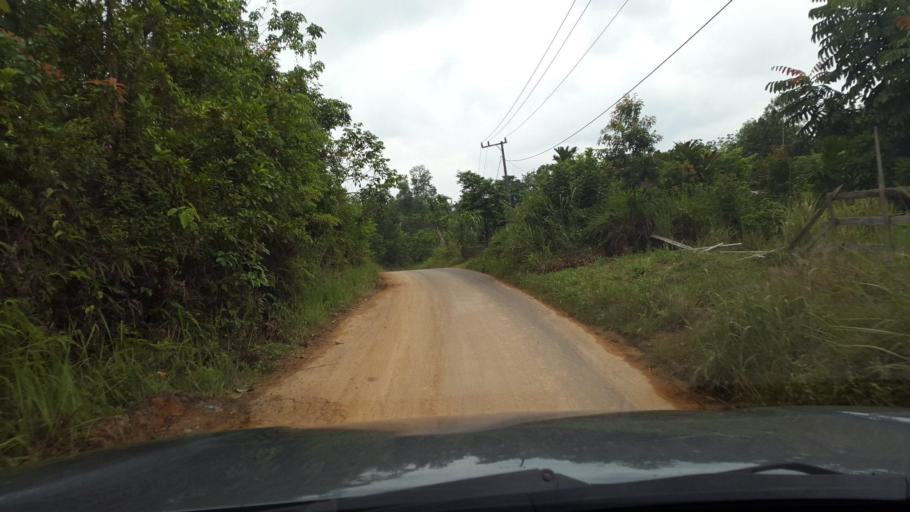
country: ID
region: South Sumatra
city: Sekayu
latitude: -3.0858
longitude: 103.7818
